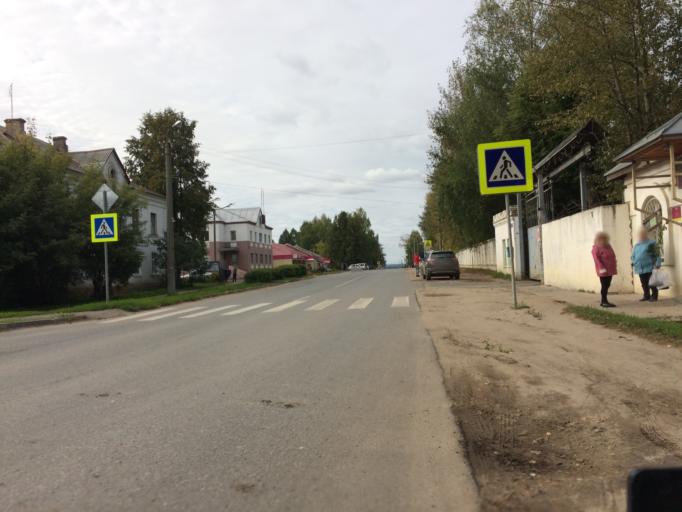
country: RU
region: Mariy-El
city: Yoshkar-Ola
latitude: 56.6533
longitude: 47.9783
